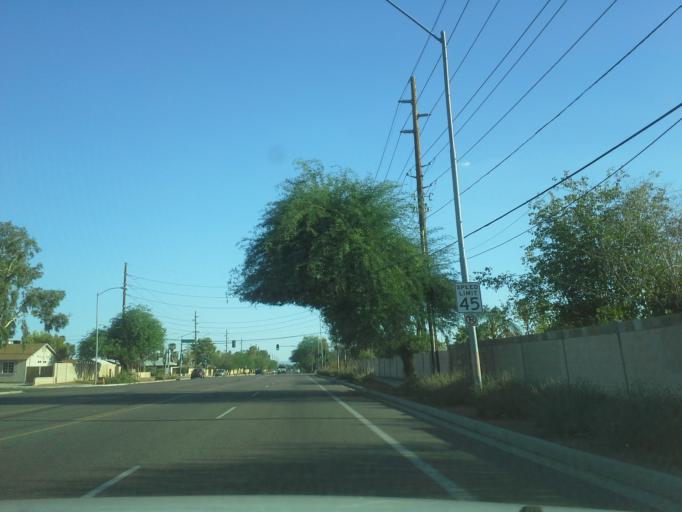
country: US
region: Arizona
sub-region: Maricopa County
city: Glendale
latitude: 33.6488
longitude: -112.1346
